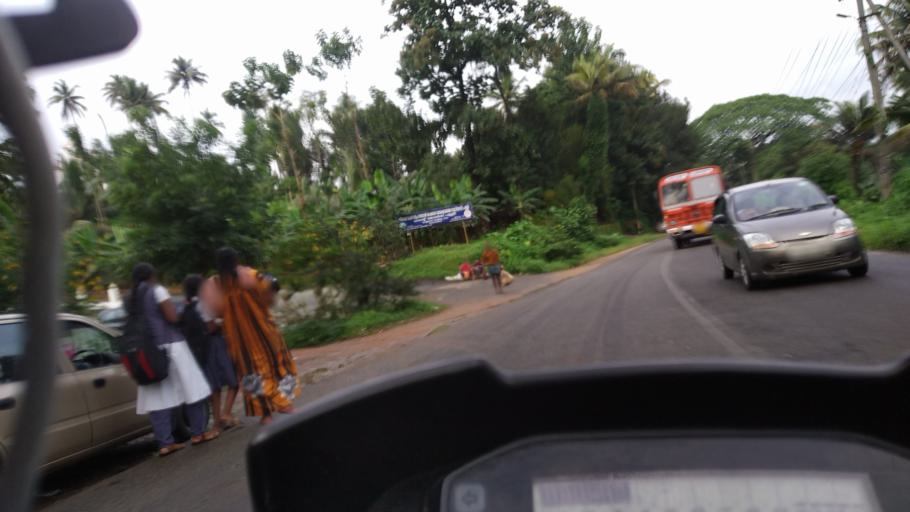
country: IN
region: Kerala
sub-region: Ernakulam
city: Kotamangalam
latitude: 10.0604
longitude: 76.6850
